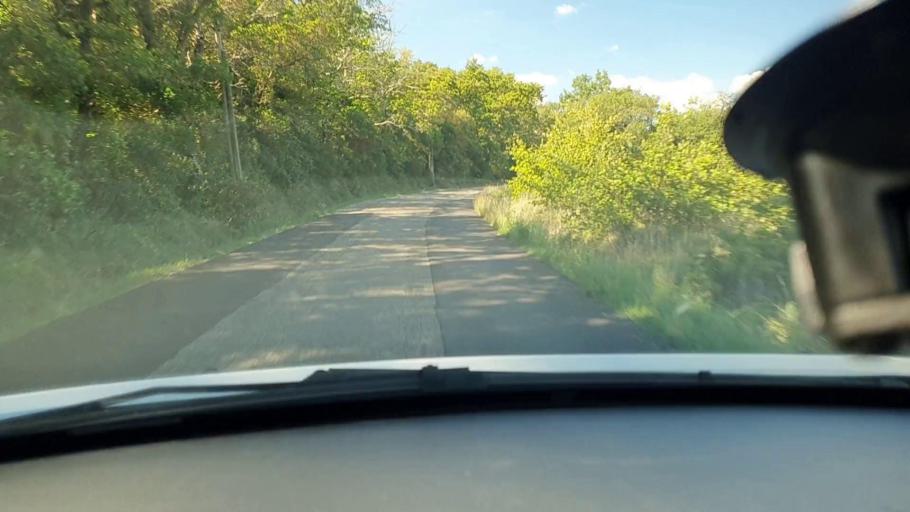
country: FR
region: Languedoc-Roussillon
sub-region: Departement du Gard
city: Sabran
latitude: 44.1747
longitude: 4.5140
